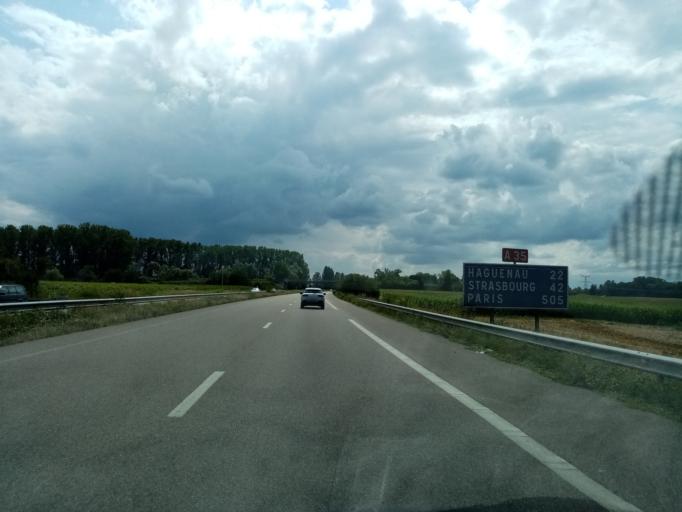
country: FR
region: Alsace
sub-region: Departement du Bas-Rhin
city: Roppenheim
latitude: 48.8500
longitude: 8.0487
